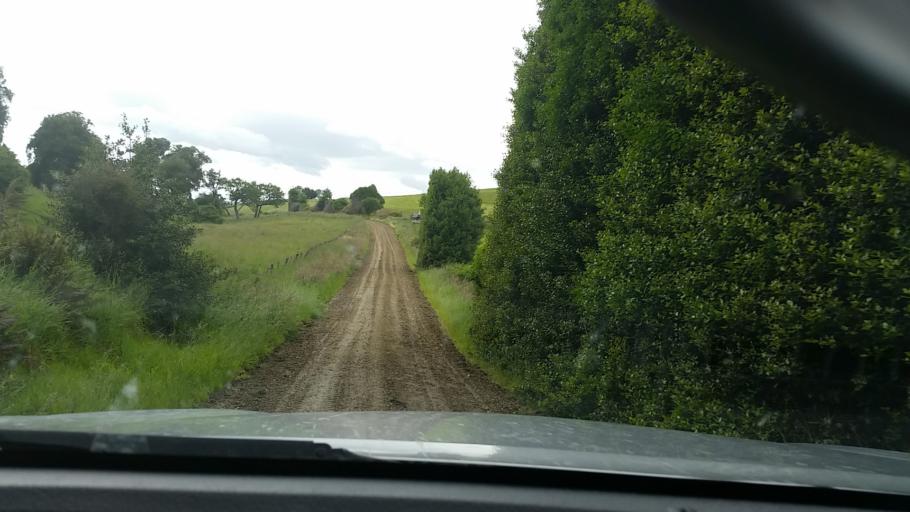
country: NZ
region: Southland
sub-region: Gore District
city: Gore
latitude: -46.2423
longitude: 168.8729
